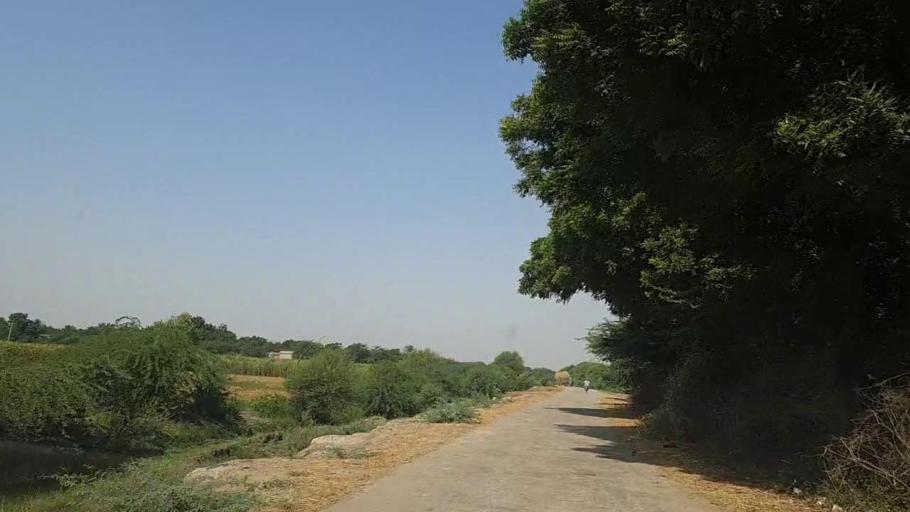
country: PK
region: Sindh
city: Daro Mehar
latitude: 24.7183
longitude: 68.1587
